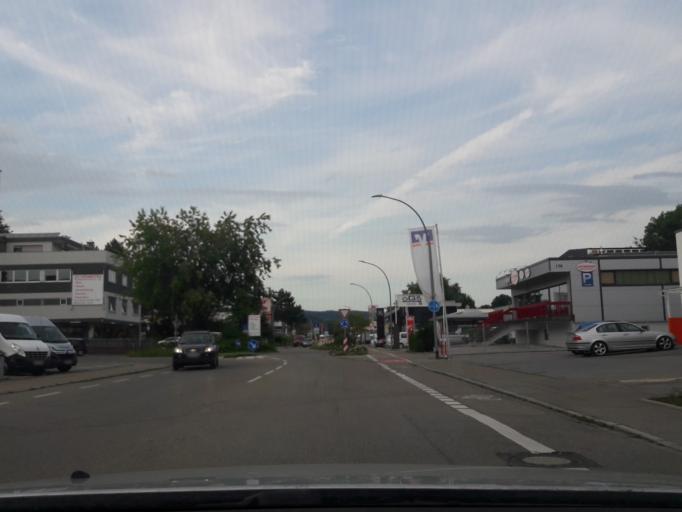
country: DE
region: Baden-Wuerttemberg
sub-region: Regierungsbezirk Stuttgart
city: Backnang
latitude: 48.9607
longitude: 9.4309
